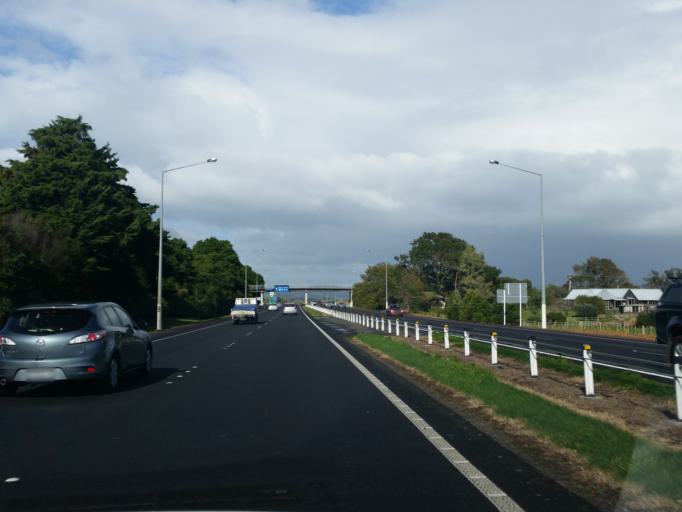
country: NZ
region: Auckland
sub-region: Auckland
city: Papakura
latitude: -37.0826
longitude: 174.9343
